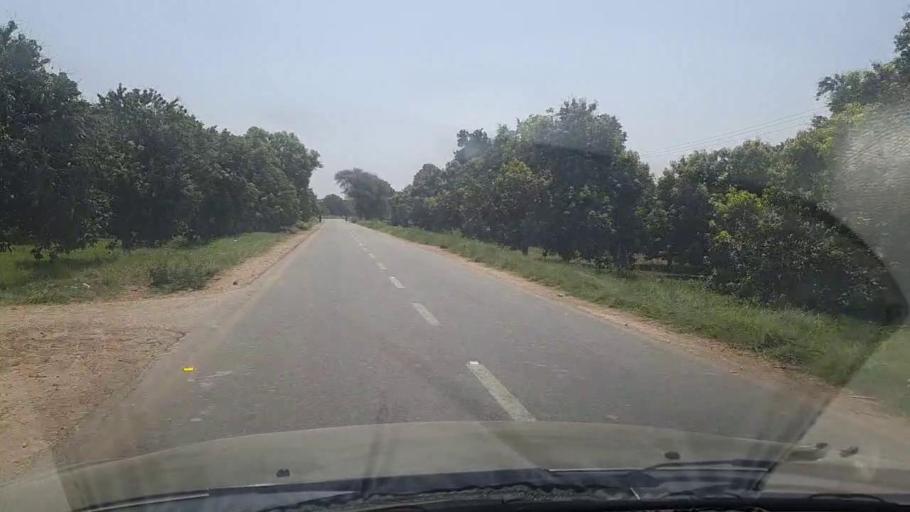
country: PK
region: Sindh
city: Tando Jam
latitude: 25.3454
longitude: 68.5167
